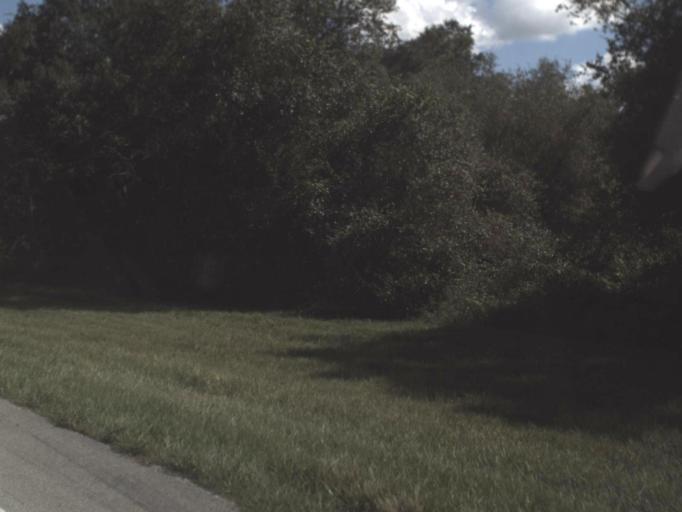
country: US
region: Florida
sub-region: Okeechobee County
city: Okeechobee
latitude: 27.3892
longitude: -81.0320
